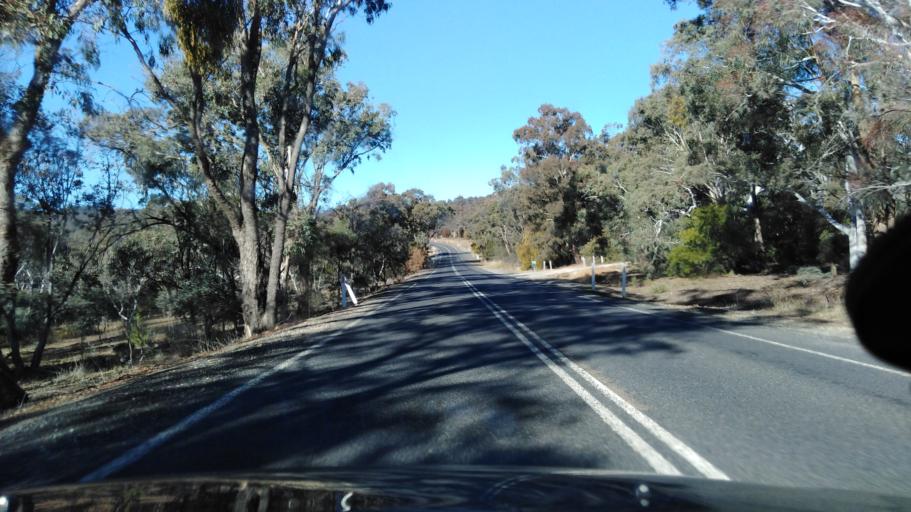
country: AU
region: New South Wales
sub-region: Yass Valley
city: Gundaroo
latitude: -35.1822
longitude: 149.2926
